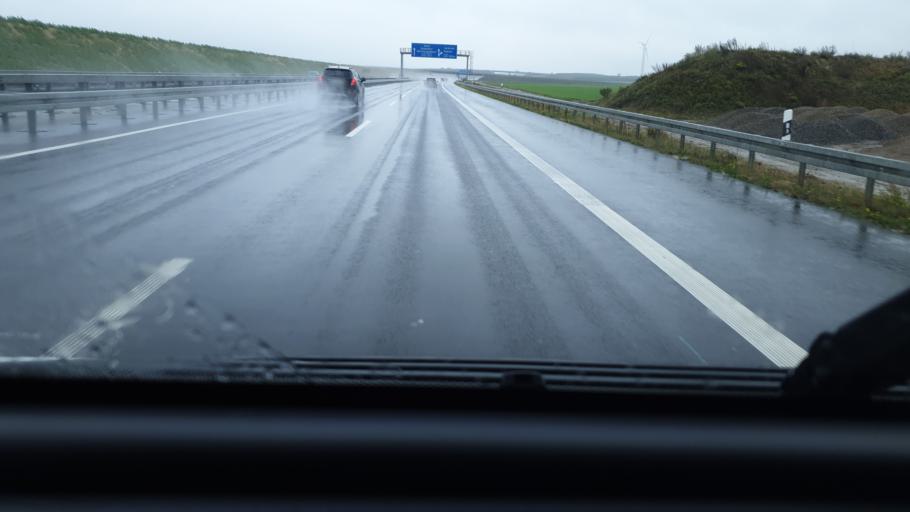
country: DE
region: North Rhine-Westphalia
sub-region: Regierungsbezirk Koln
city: Titz
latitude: 51.0256
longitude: 6.4517
